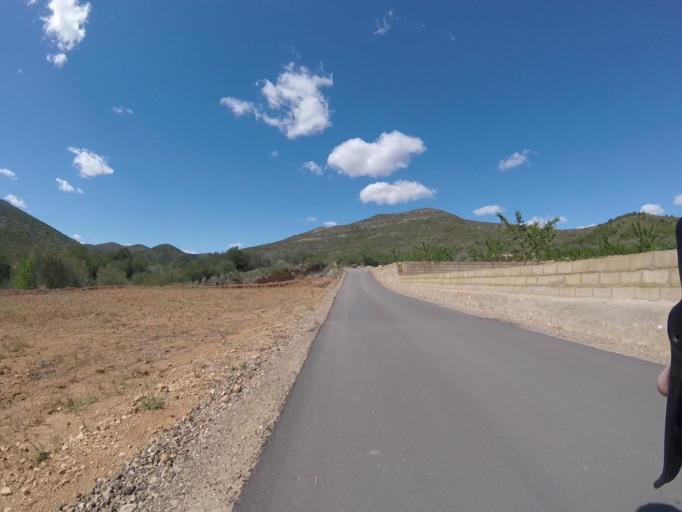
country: ES
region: Valencia
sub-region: Provincia de Castello
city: Orpesa/Oropesa del Mar
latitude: 40.1677
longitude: 0.1463
